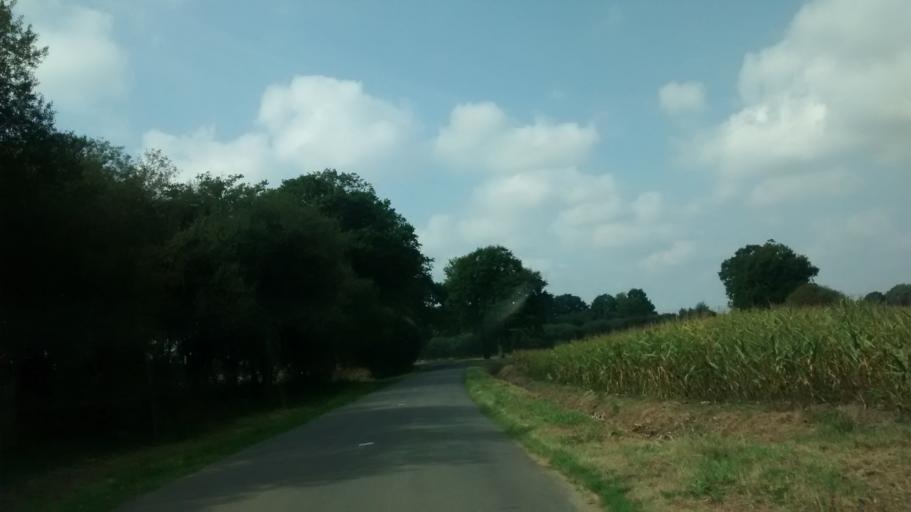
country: FR
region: Brittany
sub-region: Departement d'Ille-et-Vilaine
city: Chatillon-en-Vendelais
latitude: 48.2265
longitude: -1.2126
